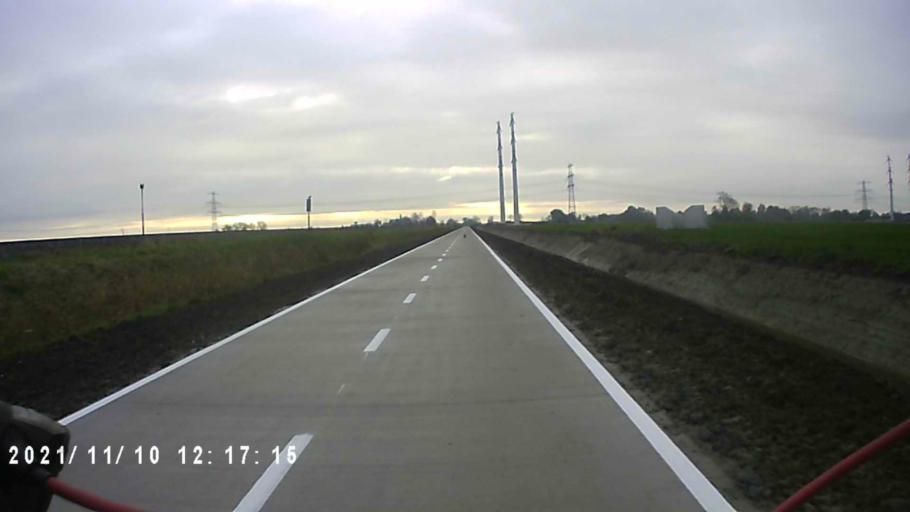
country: NL
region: Groningen
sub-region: Gemeente Winsum
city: Winsum
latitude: 53.3042
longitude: 6.5372
